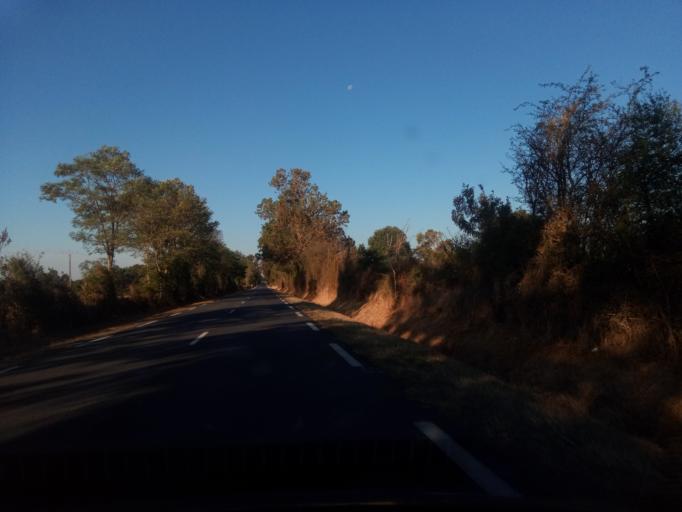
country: FR
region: Poitou-Charentes
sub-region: Departement de la Vienne
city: Montmorillon
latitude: 46.4130
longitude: 0.8239
